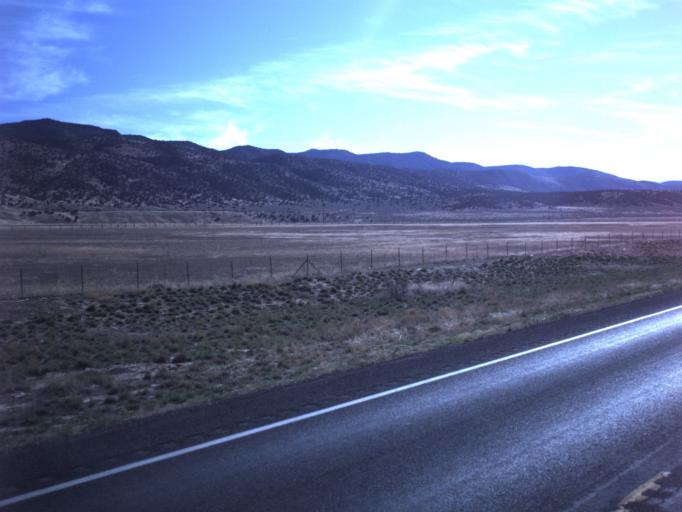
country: US
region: Utah
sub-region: Sanpete County
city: Gunnison
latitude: 39.3099
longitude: -111.8998
